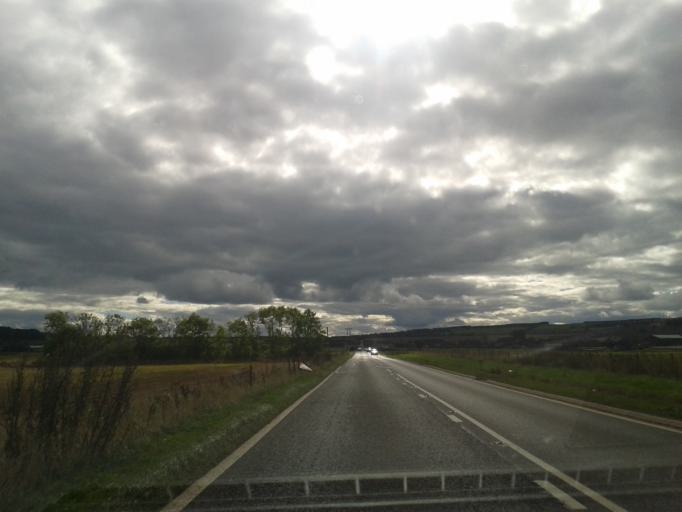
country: GB
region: Scotland
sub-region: Fife
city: Freuchie
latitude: 56.2615
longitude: -3.1432
